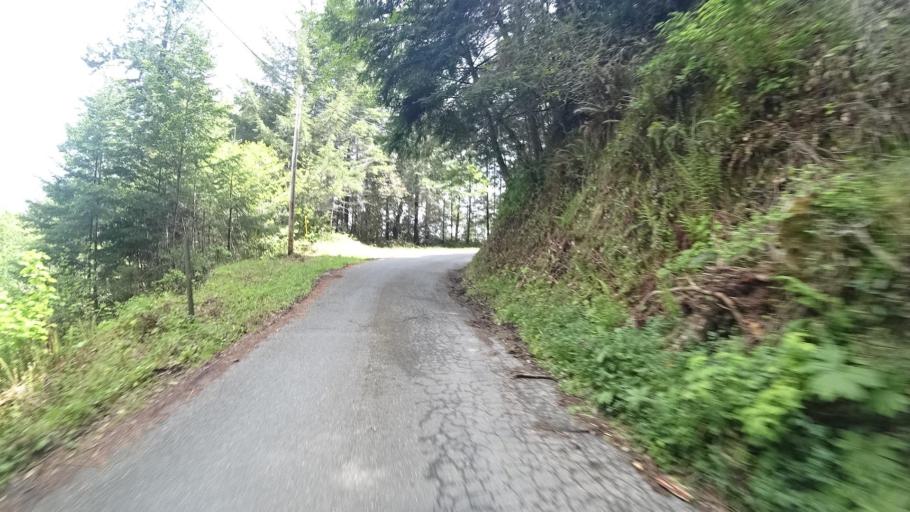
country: US
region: California
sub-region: Humboldt County
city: Blue Lake
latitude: 40.7588
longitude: -123.9136
